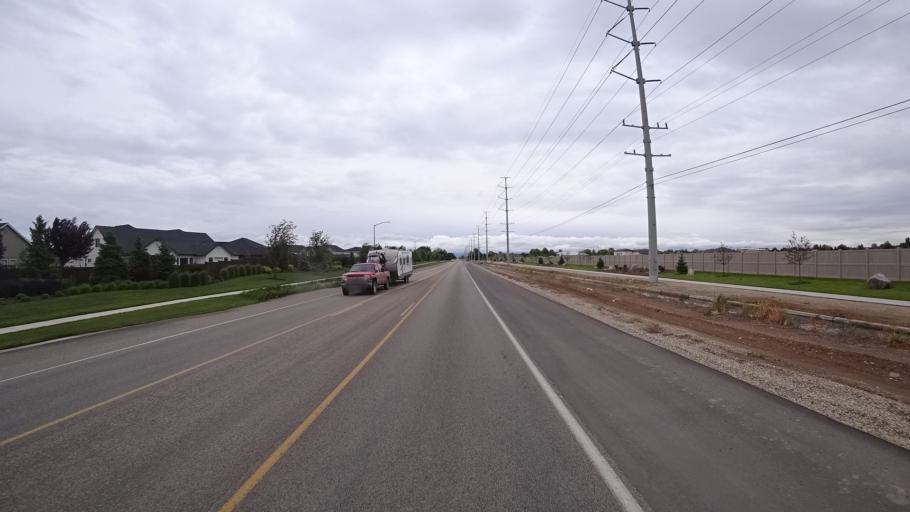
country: US
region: Idaho
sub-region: Ada County
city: Meridian
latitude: 43.6484
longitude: -116.4086
